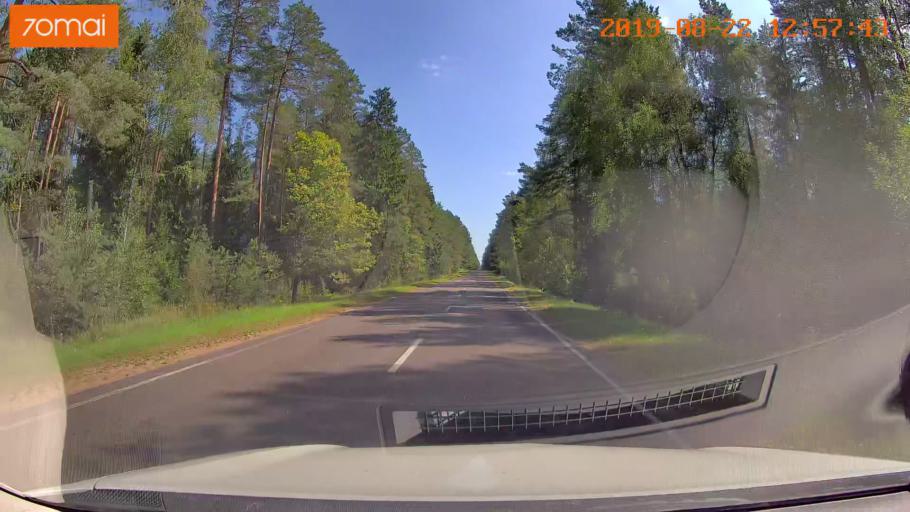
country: BY
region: Minsk
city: Prawdzinski
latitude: 53.4277
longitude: 27.7543
